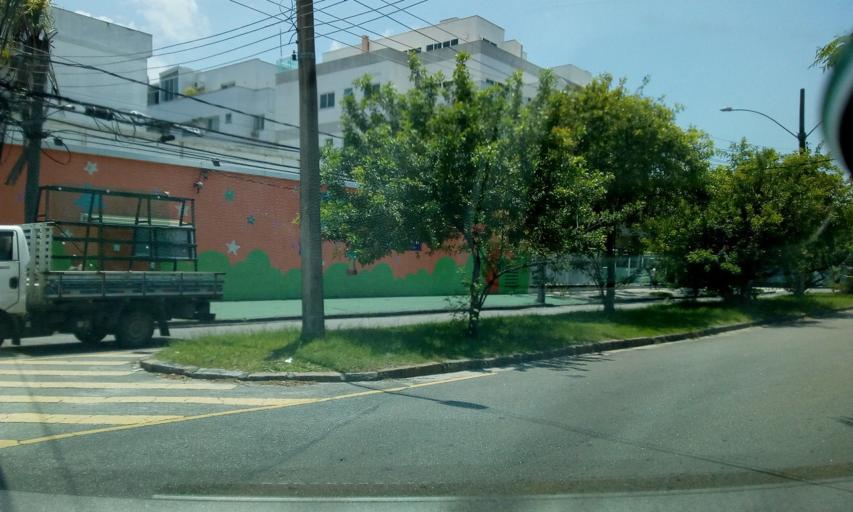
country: BR
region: Rio de Janeiro
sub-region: Nilopolis
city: Nilopolis
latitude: -23.0176
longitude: -43.4624
